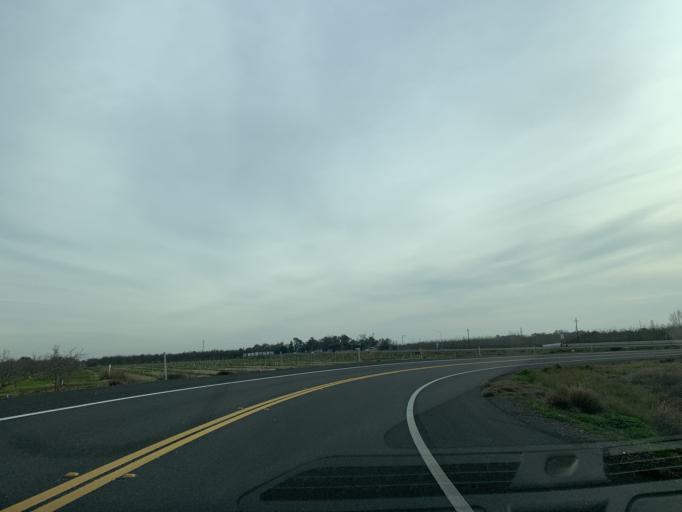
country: US
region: California
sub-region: Yuba County
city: Plumas Lake
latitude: 38.8981
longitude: -121.5805
